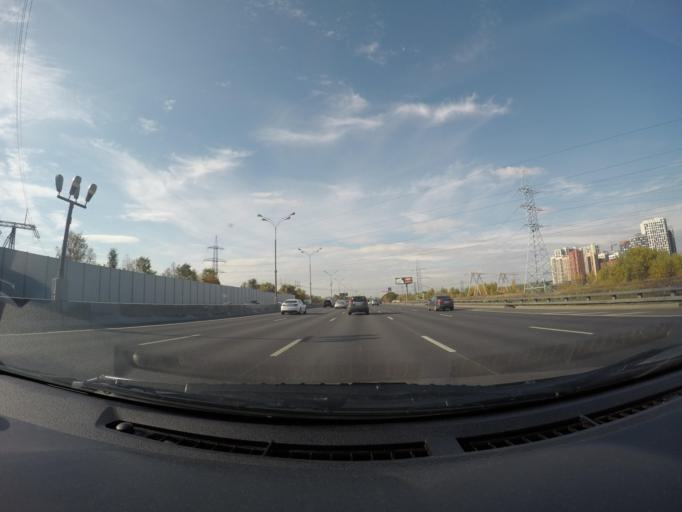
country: RU
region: Moscow
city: Kozeyevo
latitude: 55.8969
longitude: 37.6465
